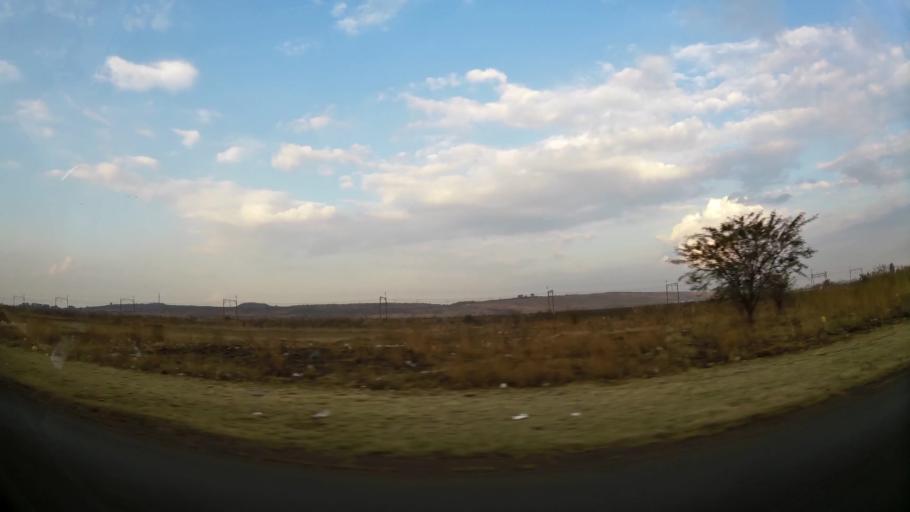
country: ZA
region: Gauteng
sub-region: City of Johannesburg Metropolitan Municipality
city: Orange Farm
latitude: -26.5916
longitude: 27.8509
